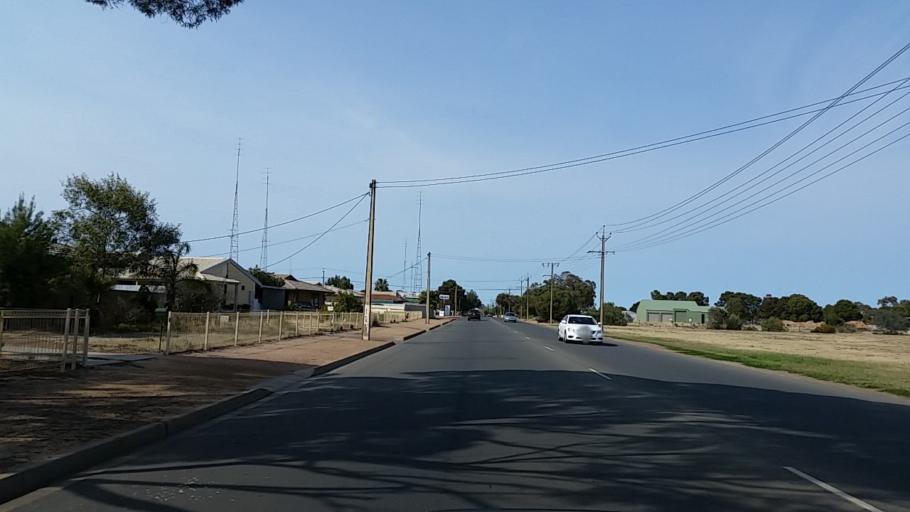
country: AU
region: South Australia
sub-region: Port Pirie City and Dists
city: Port Pirie
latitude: -33.1859
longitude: 137.9976
